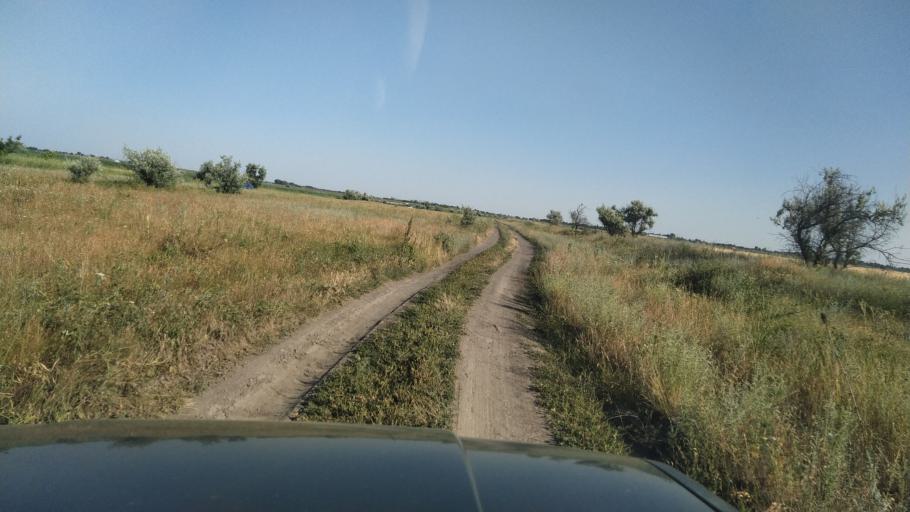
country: RU
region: Rostov
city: Kuleshovka
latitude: 47.1290
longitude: 39.6446
